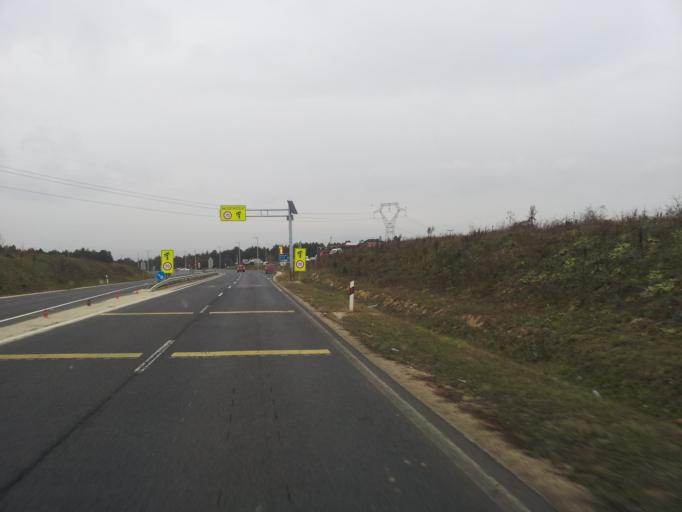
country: HU
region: Veszprem
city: Veszprem
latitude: 47.1054
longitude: 17.8676
